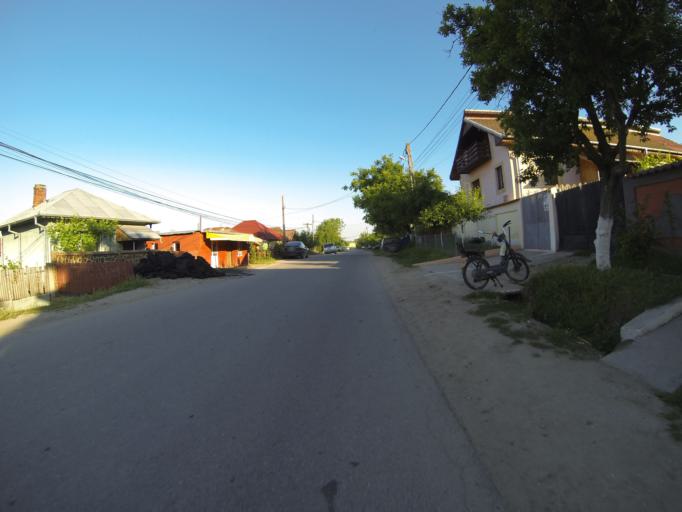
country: RO
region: Dolj
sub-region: Comuna Tuglui
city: Tuglui
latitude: 44.2051
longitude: 23.7974
